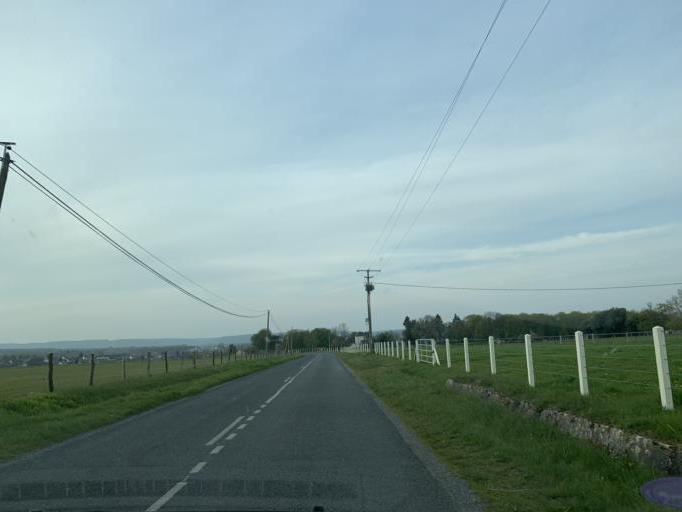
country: FR
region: Haute-Normandie
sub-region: Departement de la Seine-Maritime
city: La Mailleraye-sur-Seine
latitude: 49.4690
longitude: 0.7770
